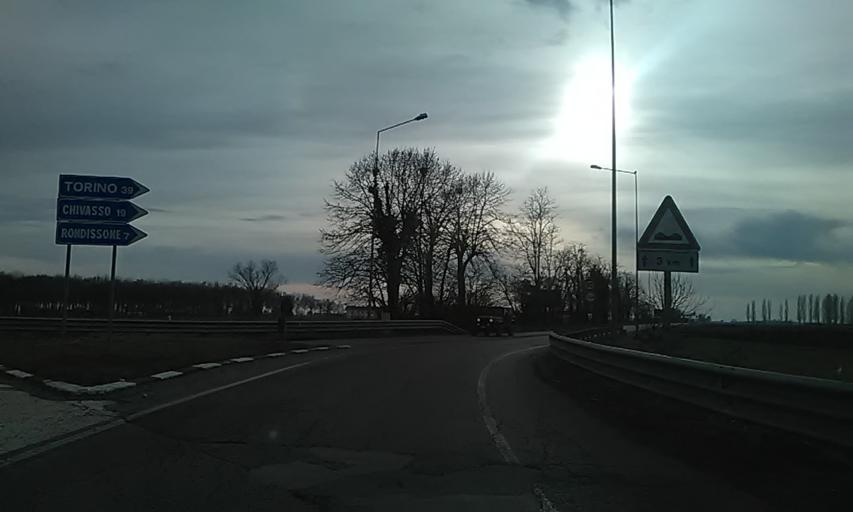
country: IT
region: Piedmont
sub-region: Provincia di Vercelli
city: Cigliano
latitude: 45.2977
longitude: 8.0056
